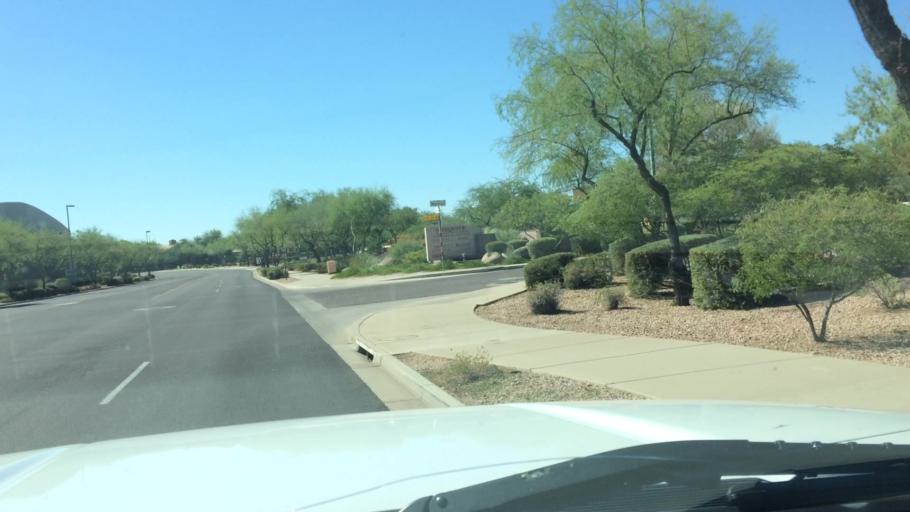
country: US
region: Arizona
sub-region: Maricopa County
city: Paradise Valley
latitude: 33.6213
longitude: -111.9311
